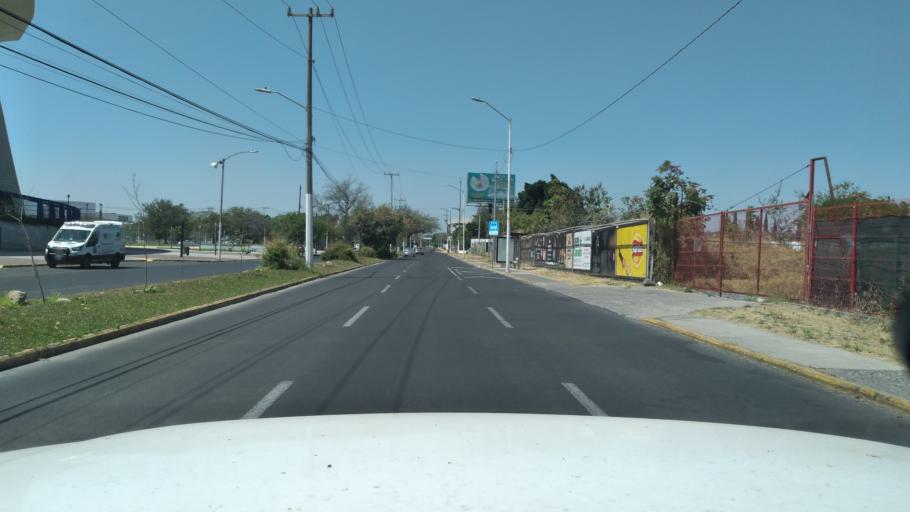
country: MX
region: Jalisco
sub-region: Zapopan
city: Zapopan
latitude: 20.7343
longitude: -103.3815
